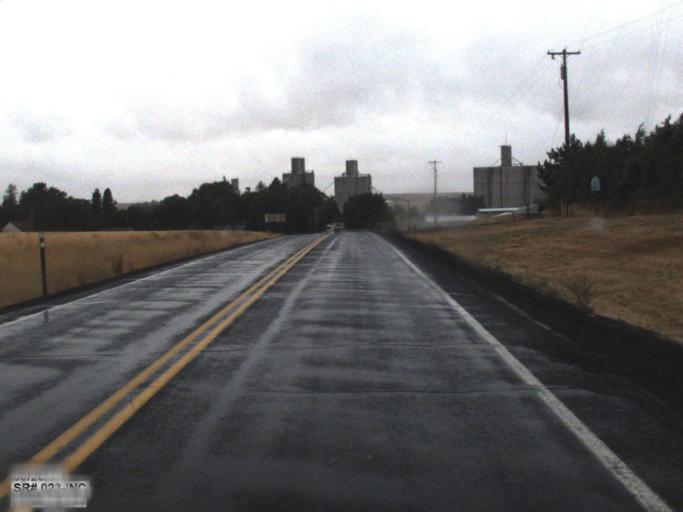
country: US
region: Washington
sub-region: Lincoln County
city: Davenport
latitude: 47.4784
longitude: -118.2454
